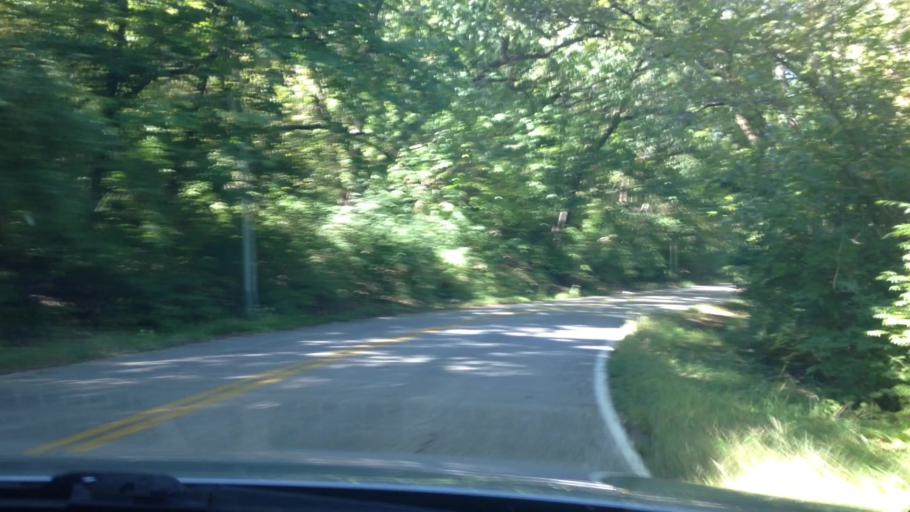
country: US
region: Missouri
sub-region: Jackson County
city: Raytown
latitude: 39.0031
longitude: -94.5135
